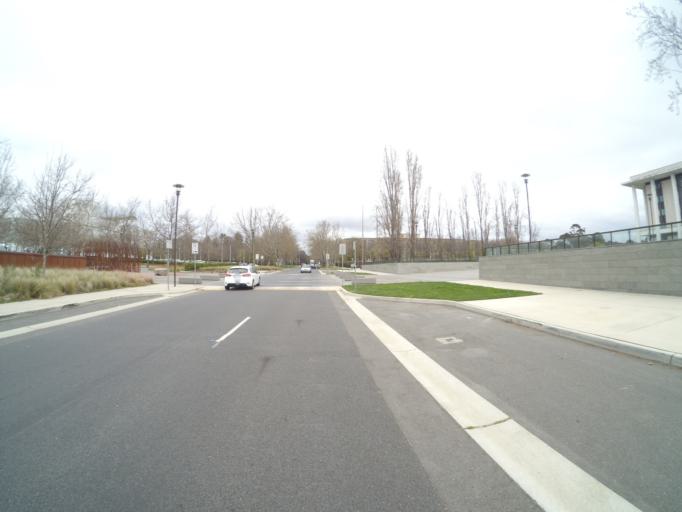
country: AU
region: Australian Capital Territory
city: Canberra
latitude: -35.2971
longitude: 149.1311
